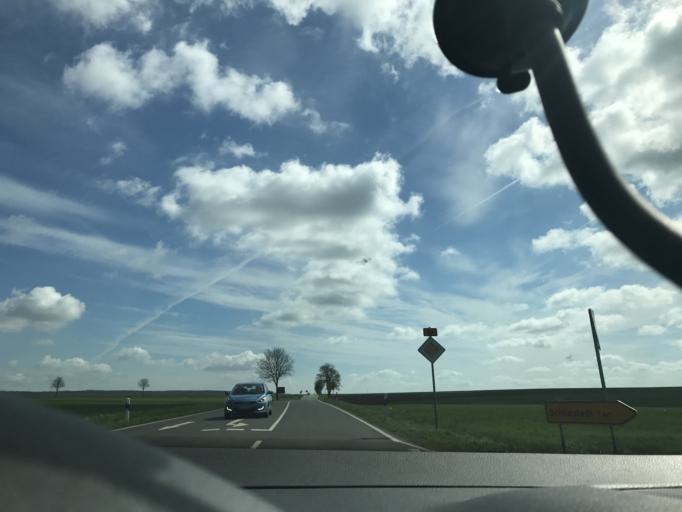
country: DE
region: Lower Saxony
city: Schoppenstedt
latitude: 52.1418
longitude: 10.8099
